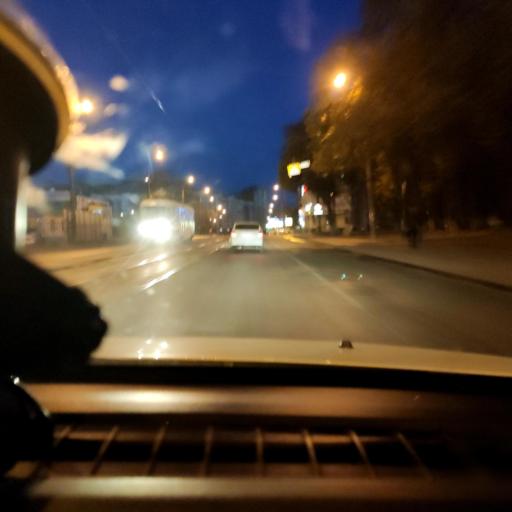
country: RU
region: Samara
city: Samara
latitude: 53.1955
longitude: 50.1604
